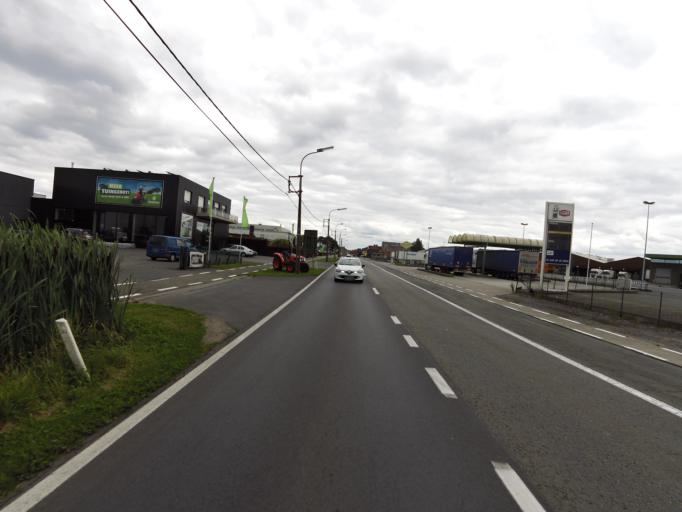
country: BE
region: Flanders
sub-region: Provincie West-Vlaanderen
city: Roeselare
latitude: 50.9505
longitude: 3.1024
